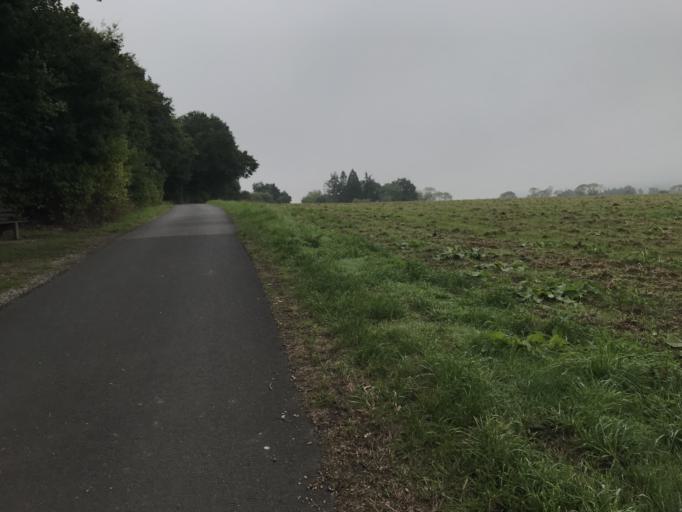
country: DE
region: Hesse
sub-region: Regierungsbezirk Kassel
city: Guxhagen
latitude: 51.2222
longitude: 9.4701
